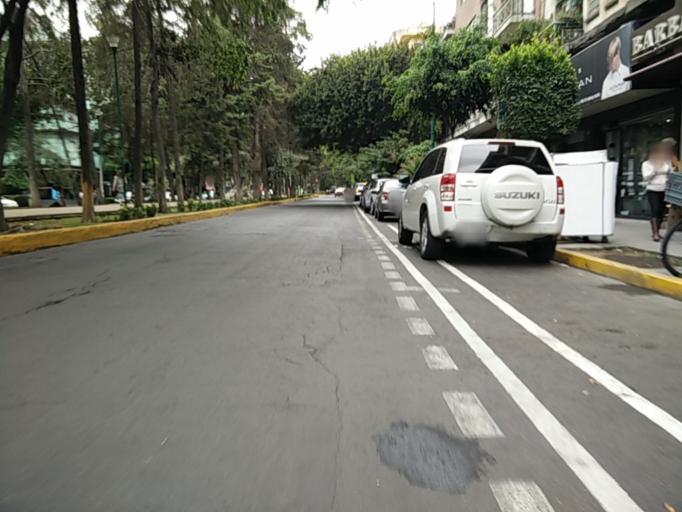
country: MX
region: Mexico City
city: Miguel Hidalgo
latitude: 19.4333
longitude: -99.1853
